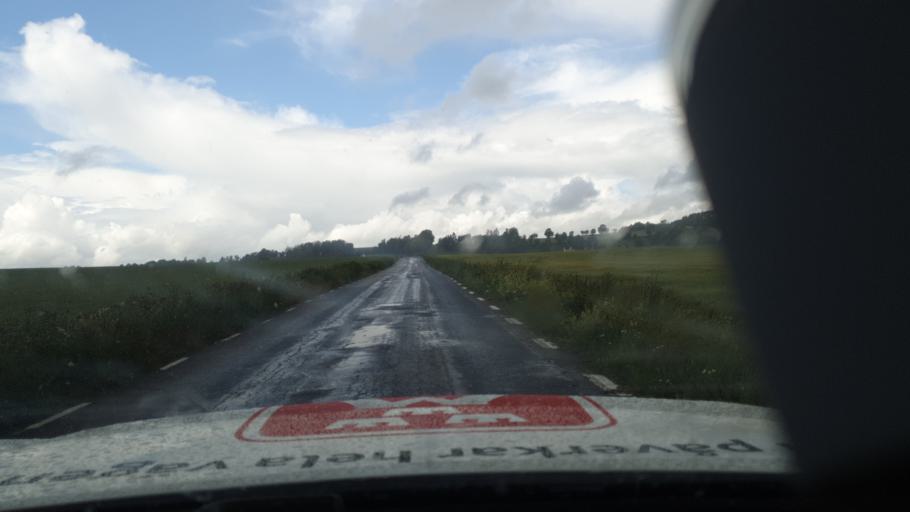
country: SE
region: Vaestra Goetaland
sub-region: Falkopings Kommun
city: Akarp
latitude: 58.1171
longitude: 13.7773
